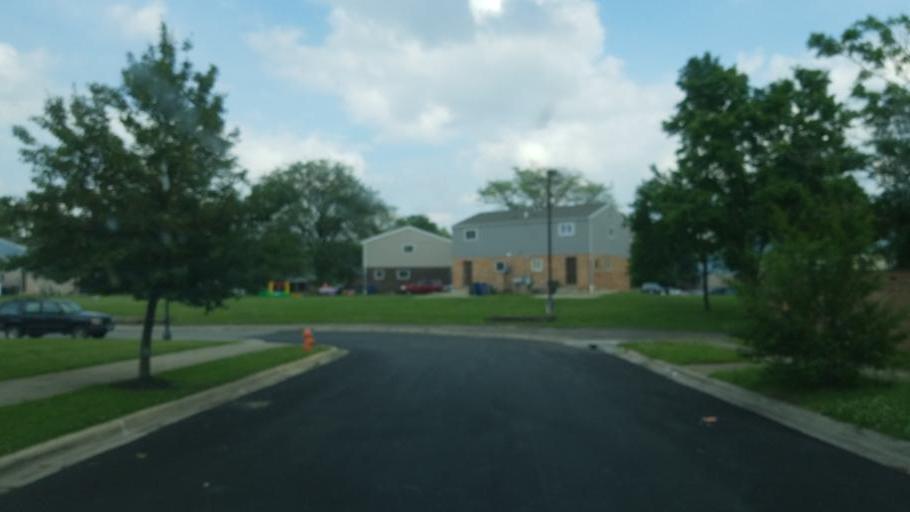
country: US
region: Ohio
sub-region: Franklin County
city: Columbus
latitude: 39.9766
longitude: -82.9753
